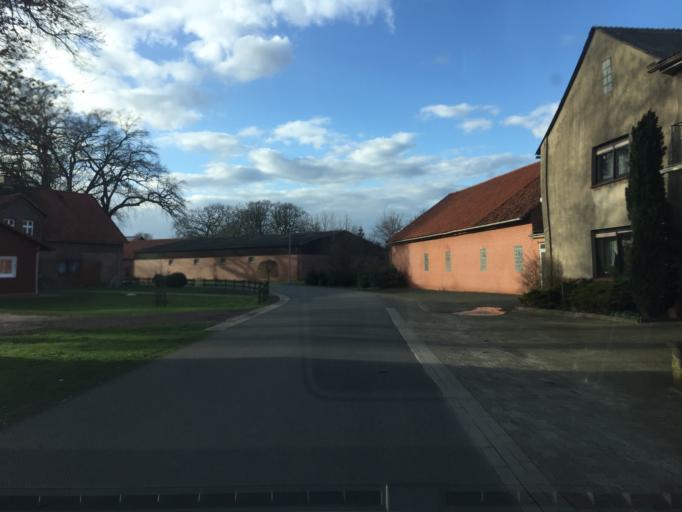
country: DE
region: Lower Saxony
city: Uchte
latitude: 52.5555
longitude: 8.9297
